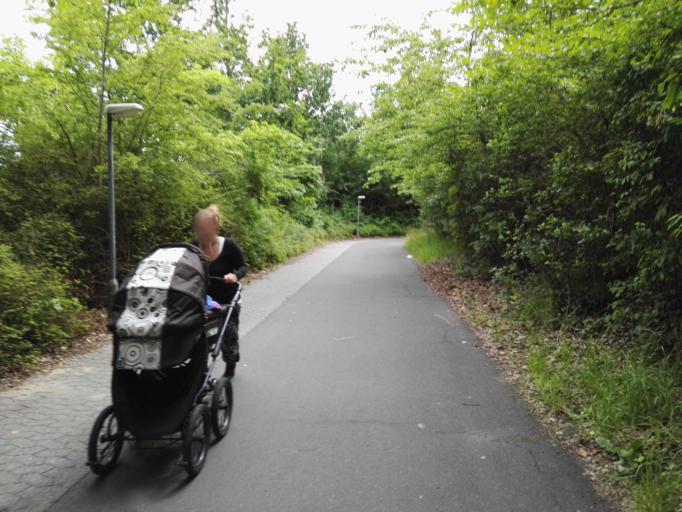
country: DK
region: Capital Region
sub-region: Ballerup Kommune
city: Malov
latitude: 55.7516
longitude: 12.3236
